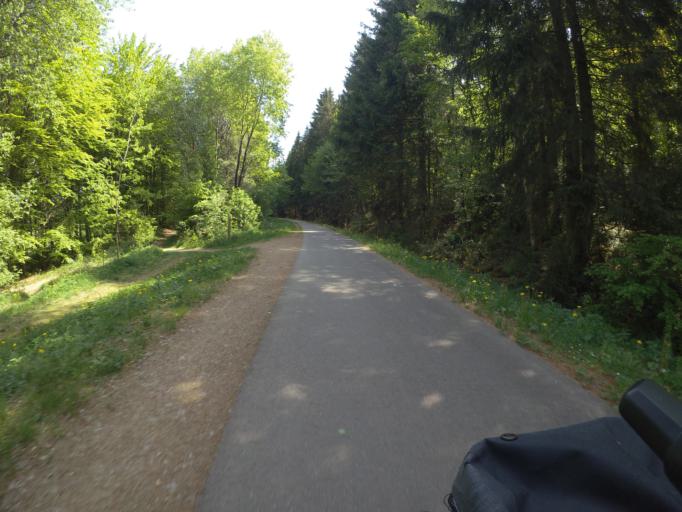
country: BE
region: Wallonia
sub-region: Province de Liege
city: Butgenbach
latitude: 50.4233
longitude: 6.2296
